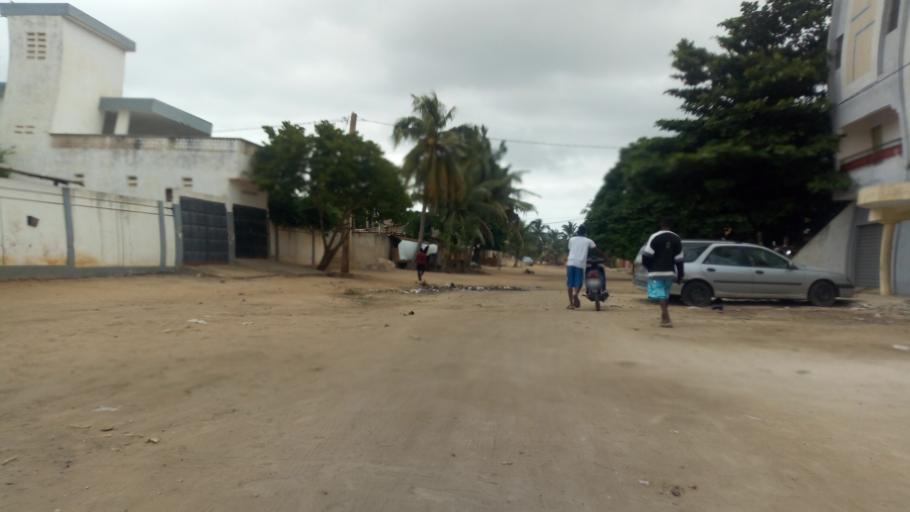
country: TG
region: Maritime
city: Lome
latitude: 6.1767
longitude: 1.1715
